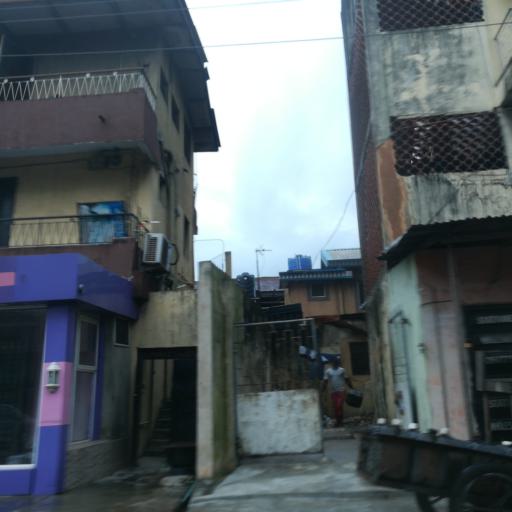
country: NG
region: Lagos
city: Ebute Metta
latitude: 6.4896
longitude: 3.3823
